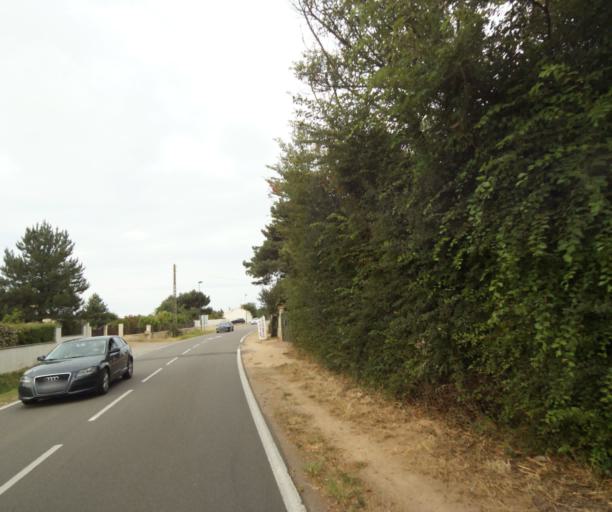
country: FR
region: Pays de la Loire
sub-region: Departement de la Vendee
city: Chateau-d'Olonne
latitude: 46.4765
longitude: -1.7190
